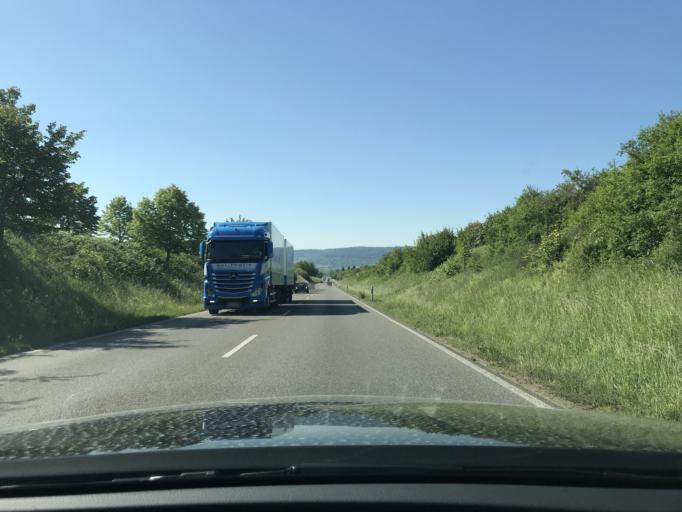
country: DE
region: Baden-Wuerttemberg
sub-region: Regierungsbezirk Stuttgart
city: Fellbach
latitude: 48.8321
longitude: 9.2891
